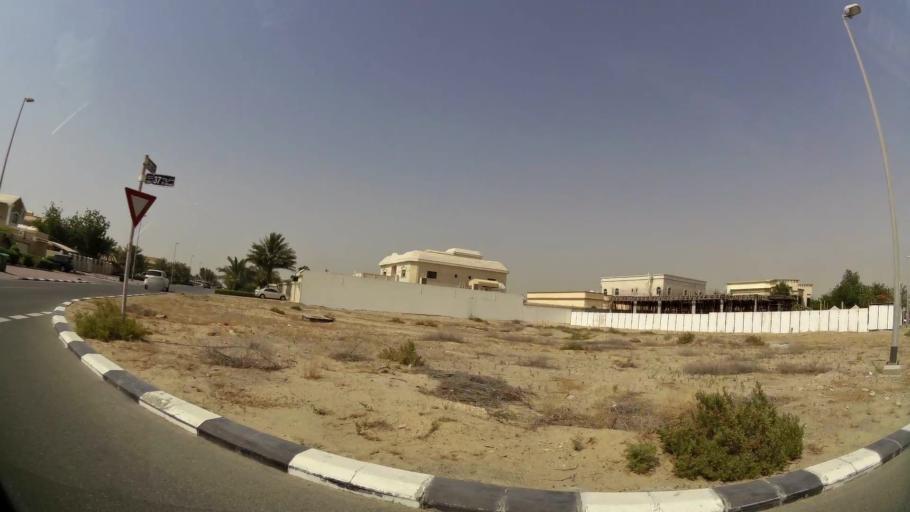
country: AE
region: Ash Shariqah
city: Sharjah
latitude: 25.2482
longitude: 55.4408
